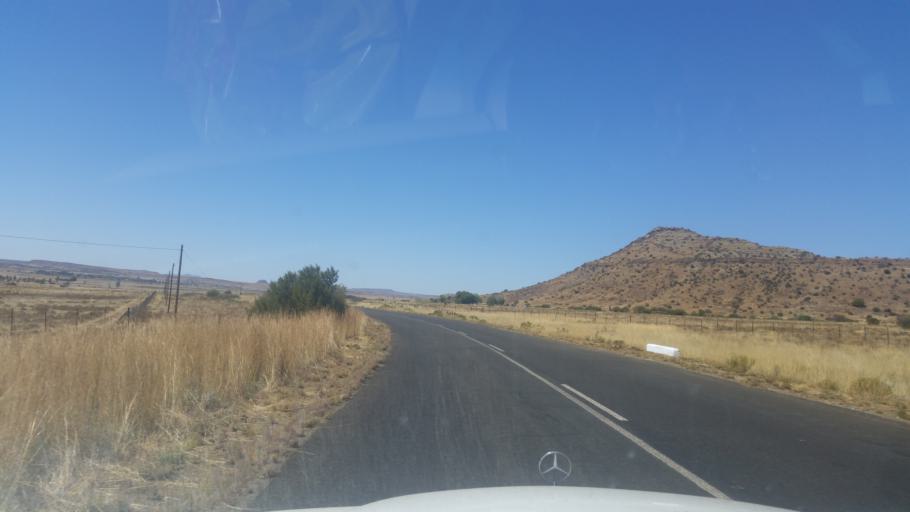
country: ZA
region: Eastern Cape
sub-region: Joe Gqabi District Municipality
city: Burgersdorp
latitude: -30.7396
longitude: 25.7550
